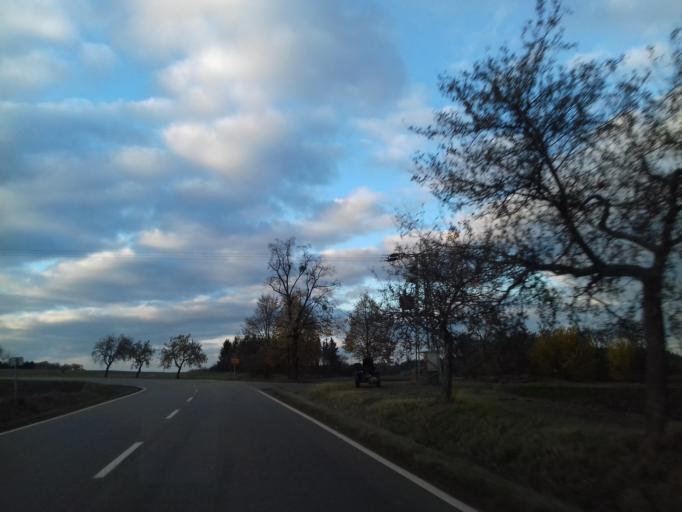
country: CZ
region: Pardubicky
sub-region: Okres Chrudim
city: Skutec
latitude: 49.8333
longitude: 16.0318
